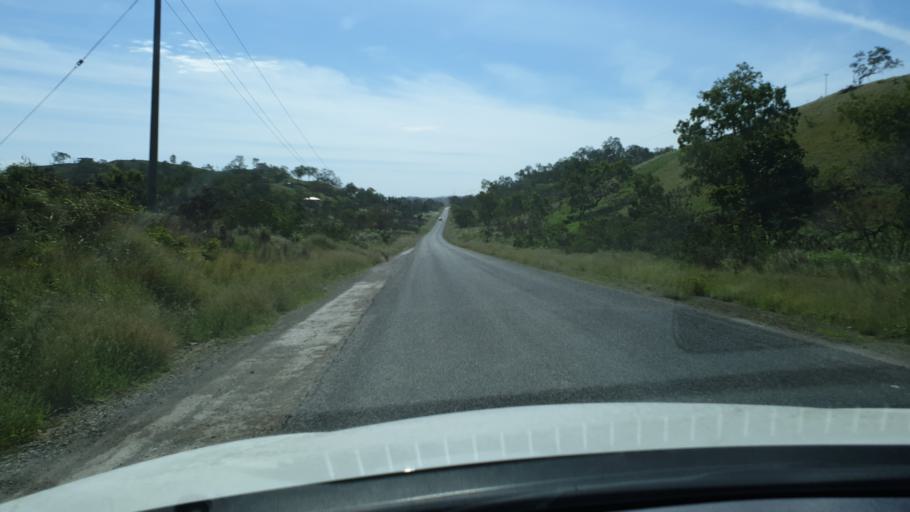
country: PG
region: National Capital
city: Port Moresby
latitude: -9.5510
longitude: 147.3396
